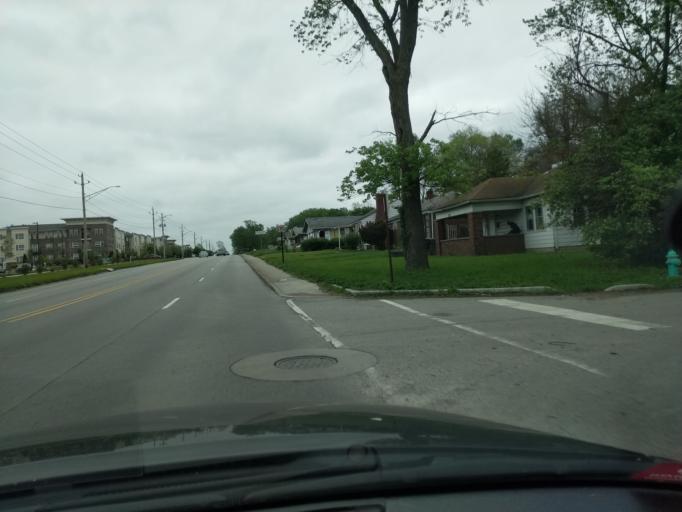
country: US
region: Indiana
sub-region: Marion County
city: Broad Ripple
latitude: 39.8253
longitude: -86.1136
